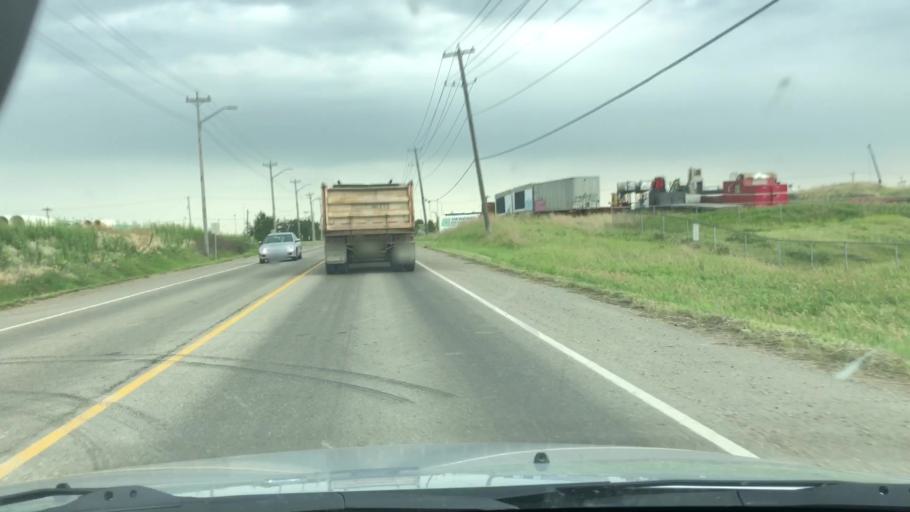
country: CA
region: Alberta
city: Sherwood Park
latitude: 53.5212
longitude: -113.3940
